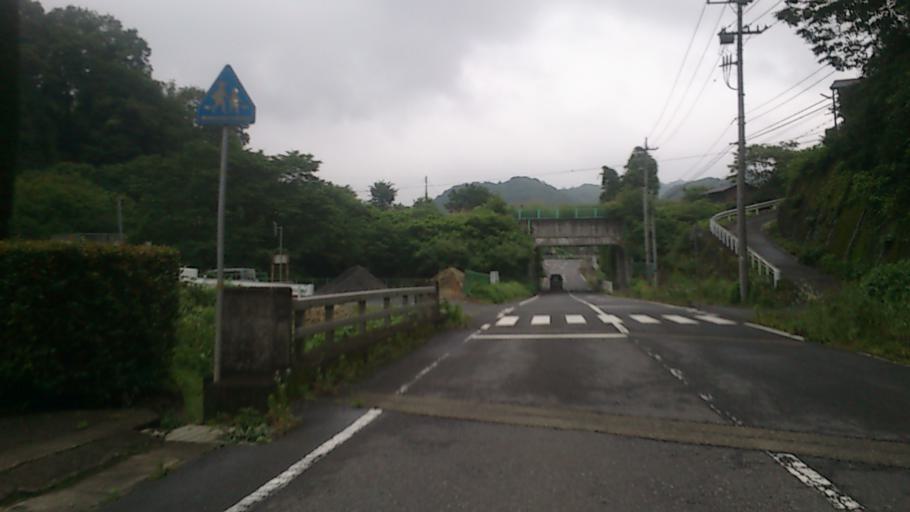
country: JP
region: Ibaraki
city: Omiya
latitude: 36.6322
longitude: 140.3932
